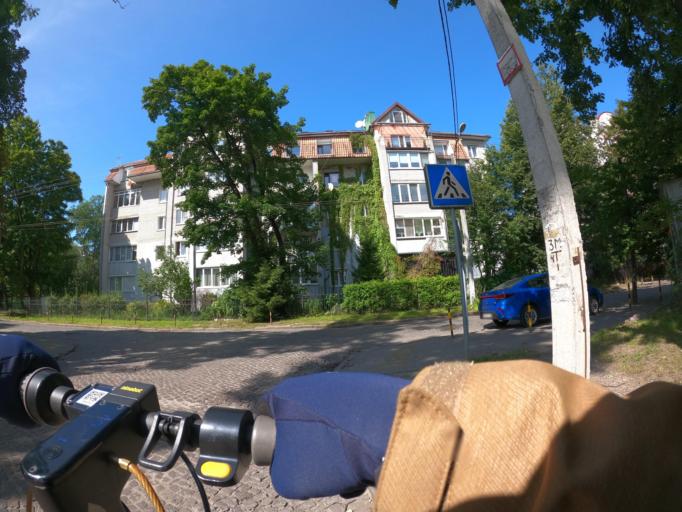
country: RU
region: Kaliningrad
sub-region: Gorod Kaliningrad
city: Kaliningrad
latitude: 54.7324
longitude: 20.5156
